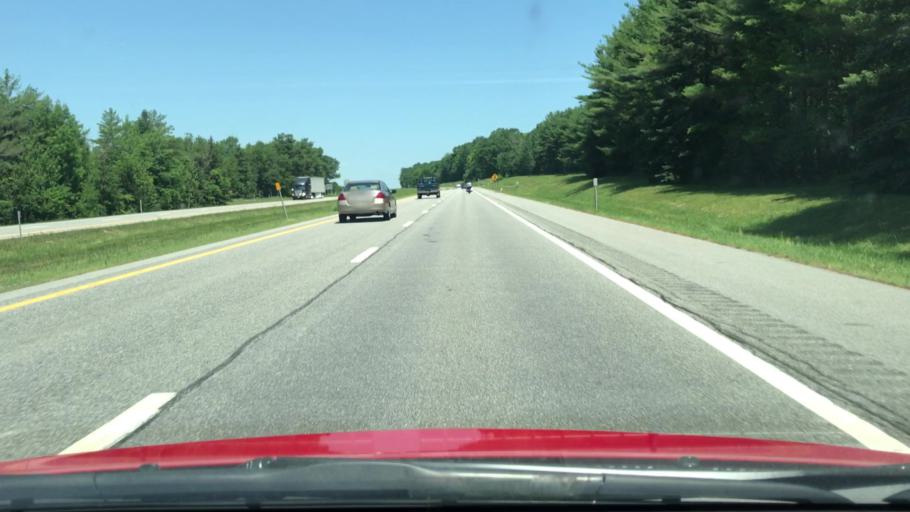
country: US
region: New York
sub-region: Essex County
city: Keeseville
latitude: 44.4446
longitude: -73.4907
